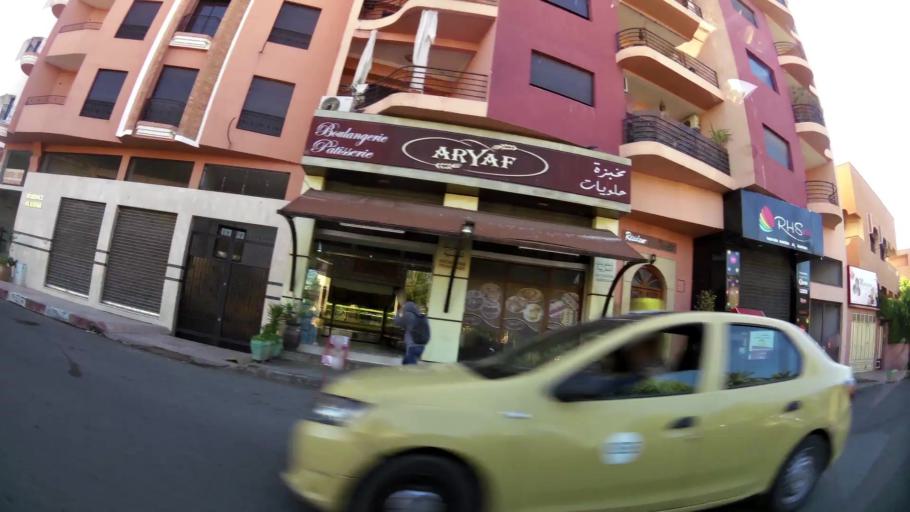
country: MA
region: Marrakech-Tensift-Al Haouz
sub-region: Marrakech
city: Marrakesh
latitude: 31.6478
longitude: -8.0142
